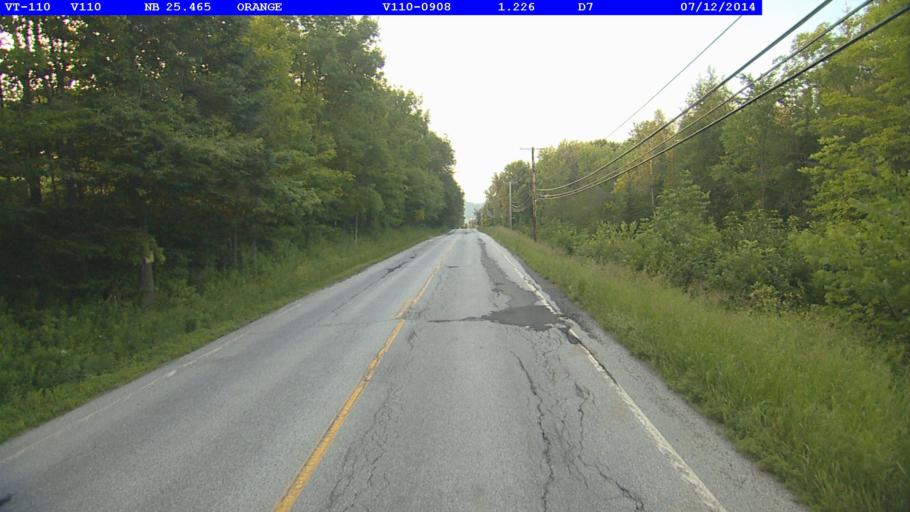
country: US
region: Vermont
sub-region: Washington County
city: South Barre
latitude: 44.1417
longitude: -72.4335
